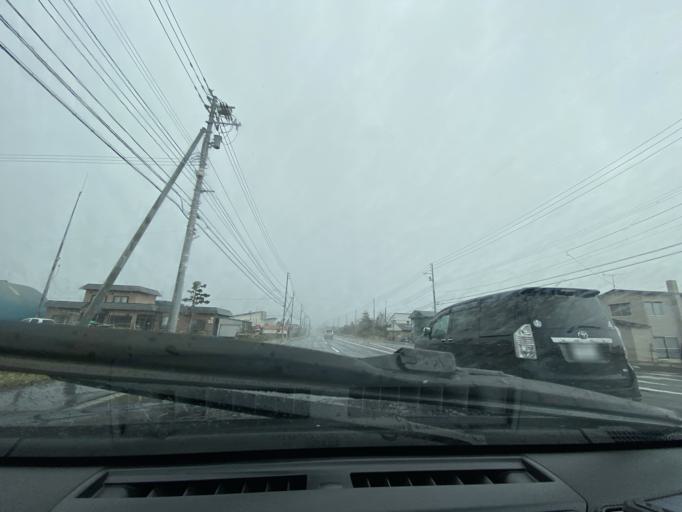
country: JP
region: Hokkaido
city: Takikawa
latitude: 43.6197
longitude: 141.9383
